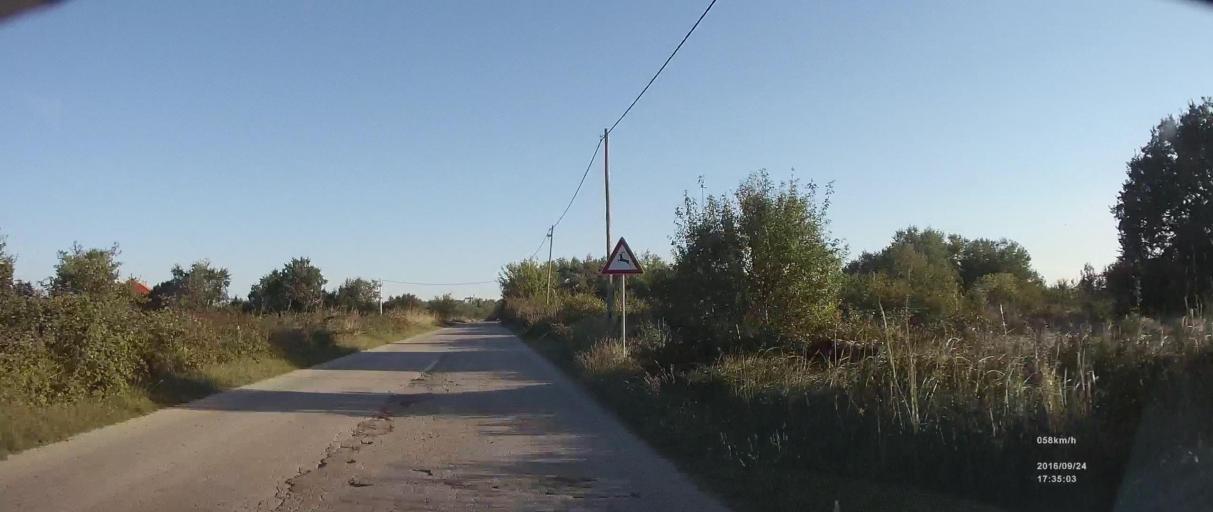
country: HR
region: Zadarska
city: Posedarje
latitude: 44.1635
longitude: 15.4648
